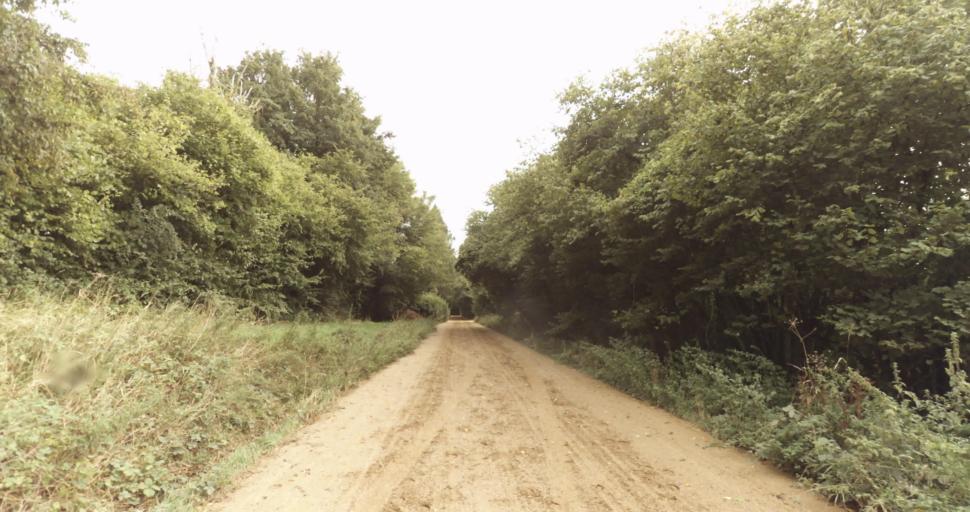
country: FR
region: Lower Normandy
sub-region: Departement de l'Orne
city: Sainte-Gauburge-Sainte-Colombe
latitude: 48.7533
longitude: 0.3713
